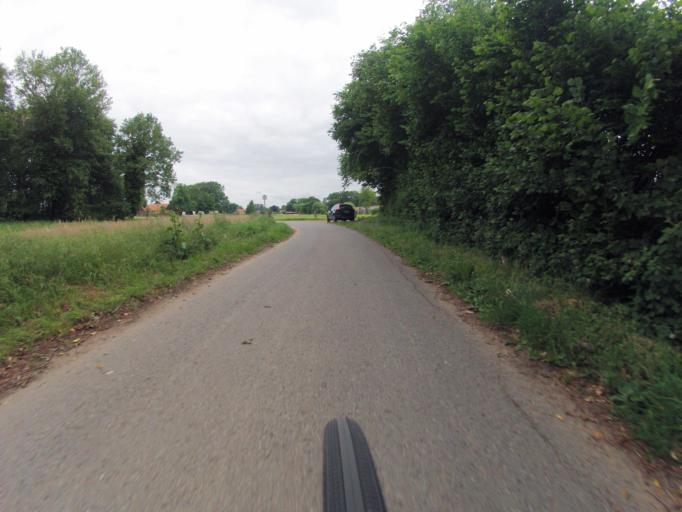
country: DE
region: North Rhine-Westphalia
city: Emsdetten
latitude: 52.1661
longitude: 7.5742
